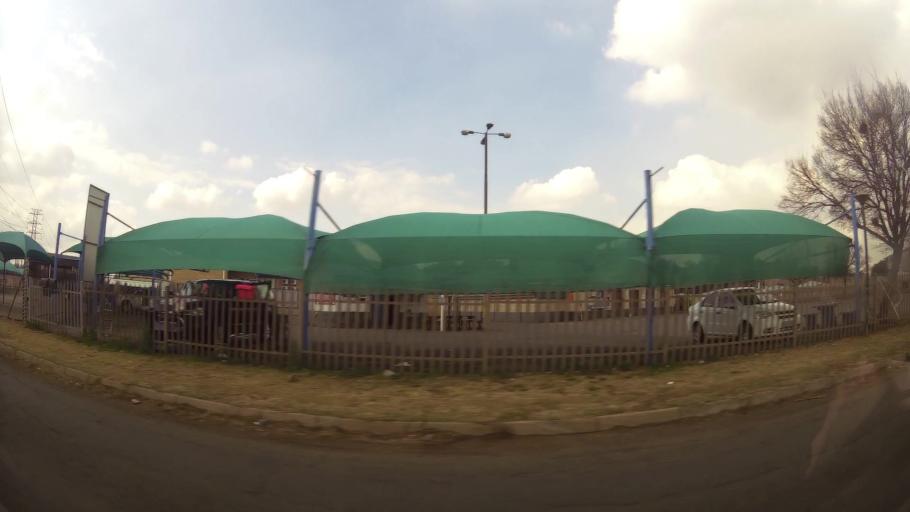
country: ZA
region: Gauteng
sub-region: Sedibeng District Municipality
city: Vereeniging
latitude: -26.6703
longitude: 27.9393
